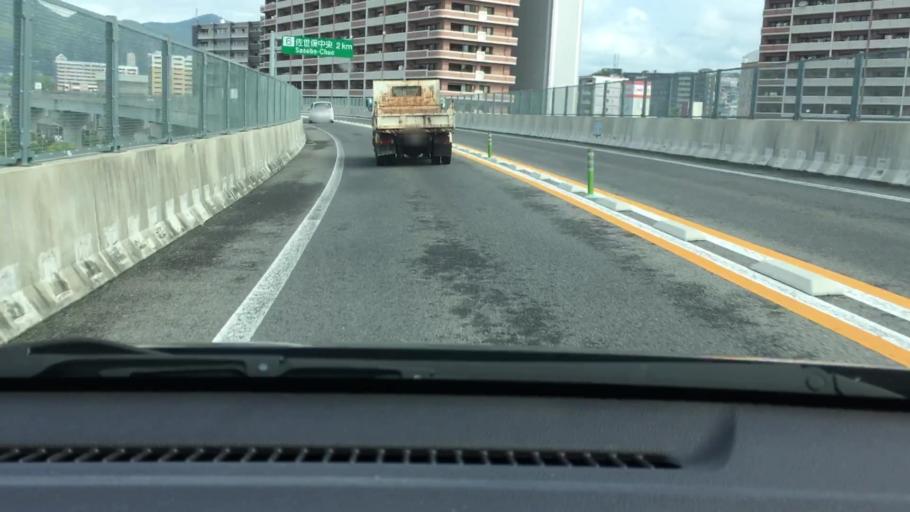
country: JP
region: Nagasaki
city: Sasebo
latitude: 33.1609
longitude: 129.7284
